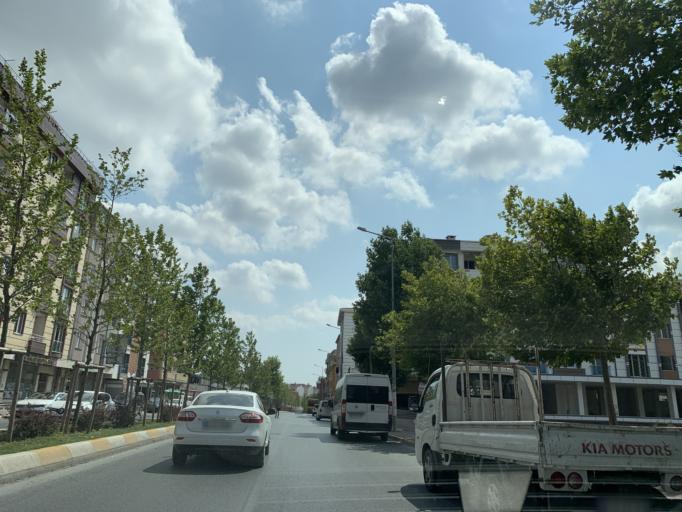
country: TR
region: Istanbul
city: Esenyurt
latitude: 41.0476
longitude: 28.6702
